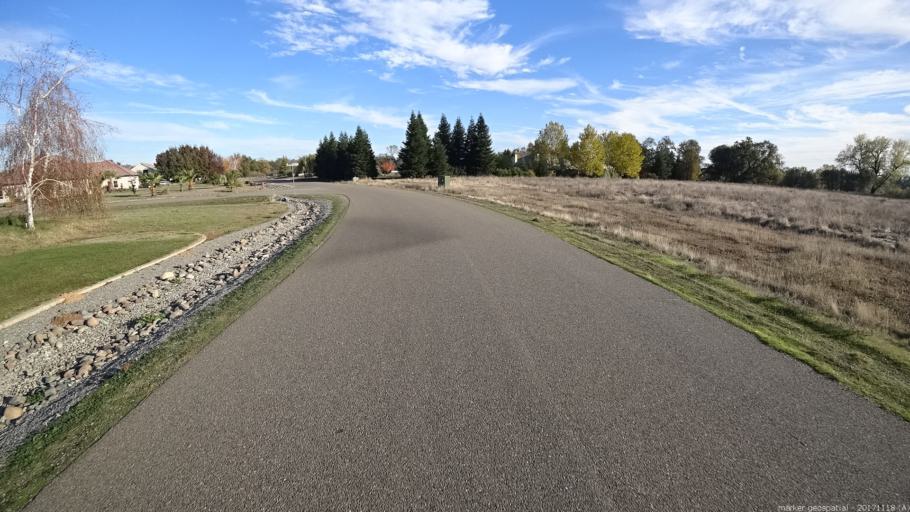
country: US
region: California
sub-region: Shasta County
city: Cottonwood
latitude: 40.3756
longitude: -122.3338
